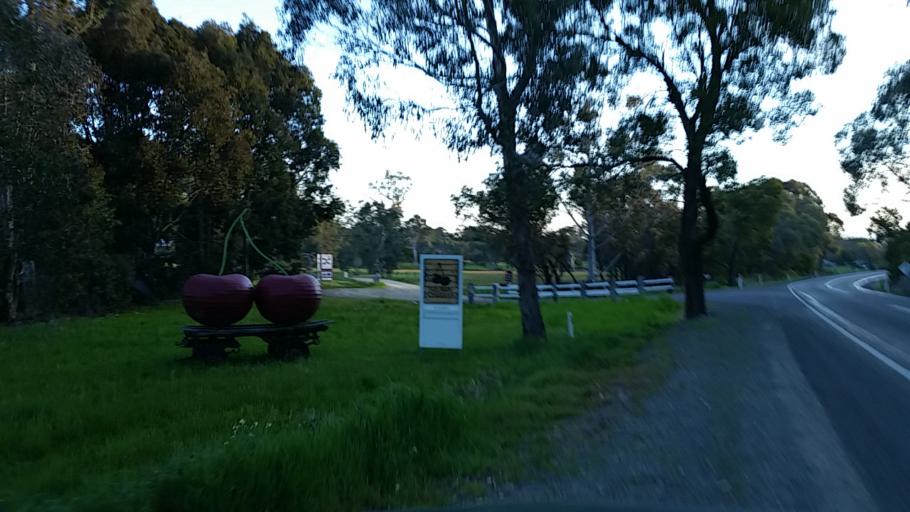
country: AU
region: South Australia
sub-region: Alexandrina
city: Mount Compass
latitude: -35.3167
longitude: 138.5673
